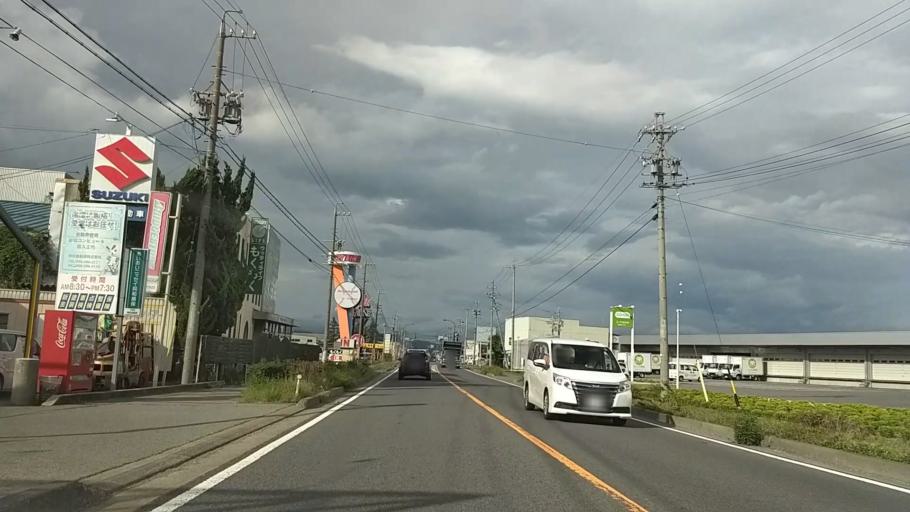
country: JP
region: Nagano
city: Suzaka
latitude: 36.6667
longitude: 138.2634
